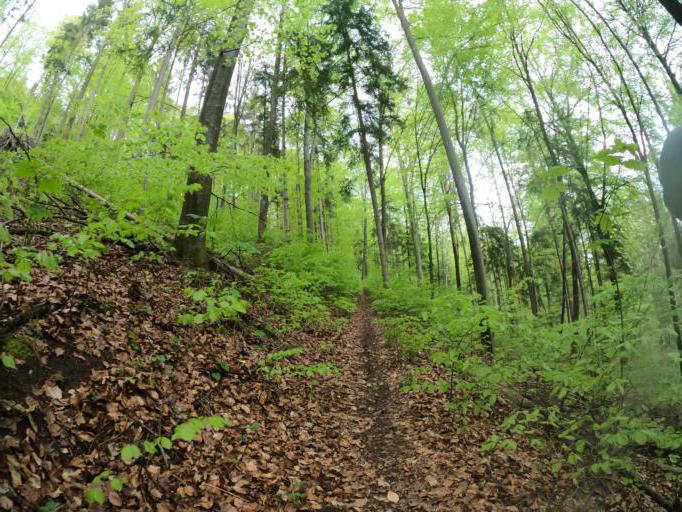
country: DE
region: Baden-Wuerttemberg
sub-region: Karlsruhe Region
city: Rohrdorf
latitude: 48.5531
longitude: 8.7048
